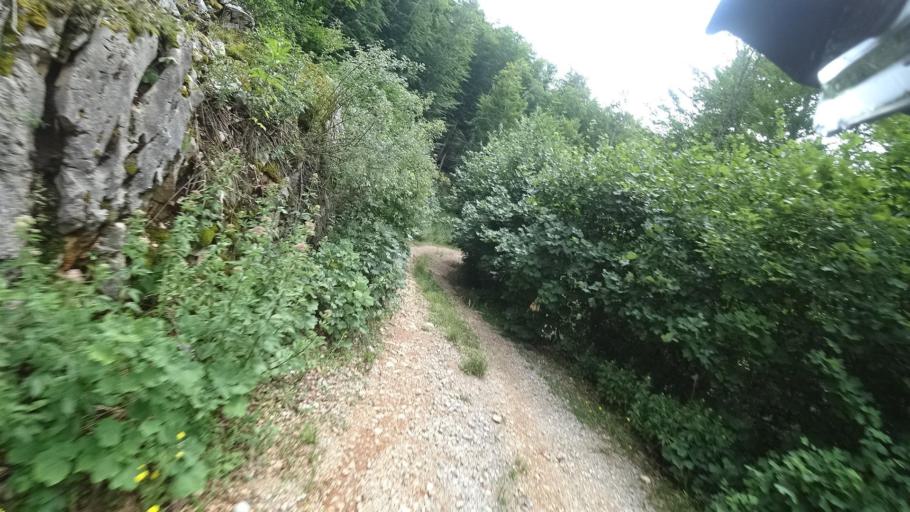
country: BA
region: Federation of Bosnia and Herzegovina
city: Bihac
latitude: 44.6391
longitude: 15.7724
